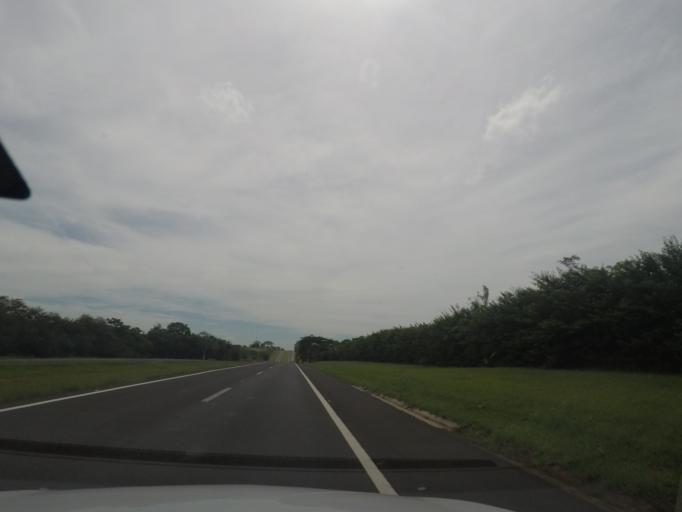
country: BR
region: Sao Paulo
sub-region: Bebedouro
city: Bebedouro
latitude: -20.9758
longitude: -48.4384
